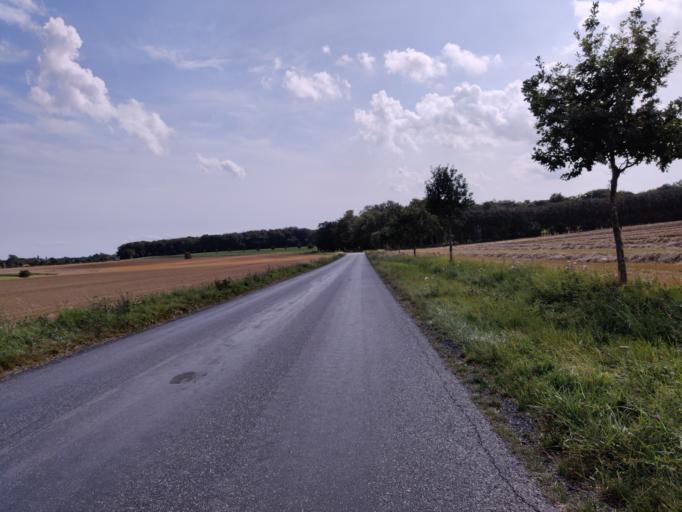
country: DK
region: Zealand
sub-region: Guldborgsund Kommune
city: Nykobing Falster
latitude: 54.6511
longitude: 11.8876
